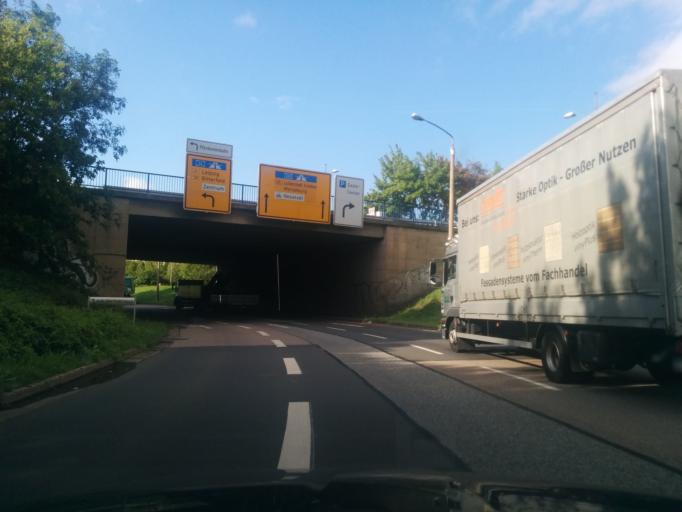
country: DE
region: Saxony-Anhalt
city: Halle Neustadt
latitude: 51.4820
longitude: 11.9444
